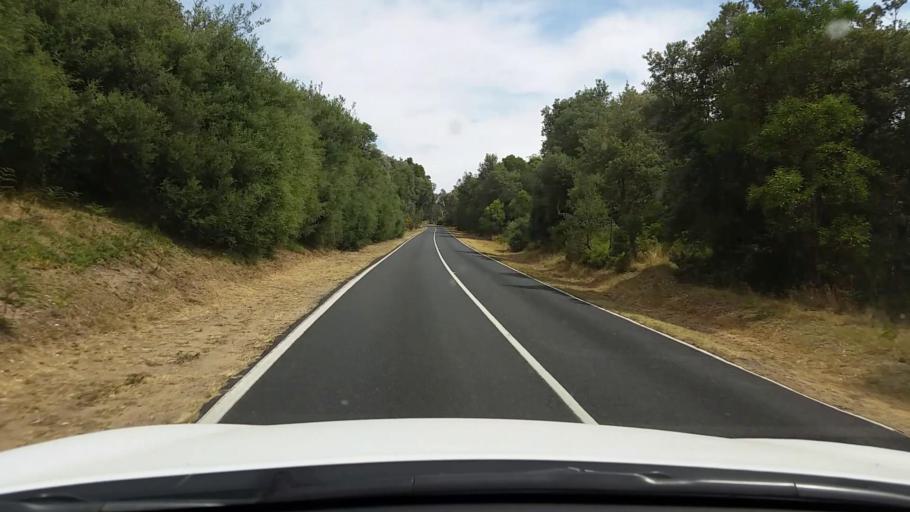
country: AU
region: Victoria
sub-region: Mornington Peninsula
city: Saint Andrews Beach
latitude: -38.4723
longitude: 144.9260
